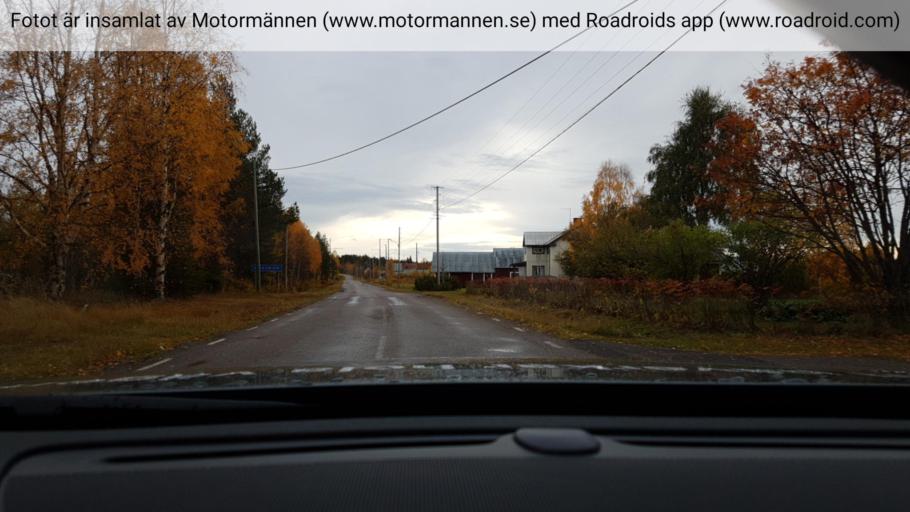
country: SE
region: Norrbotten
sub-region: Pajala Kommun
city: Pajala
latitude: 67.1741
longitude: 22.6491
